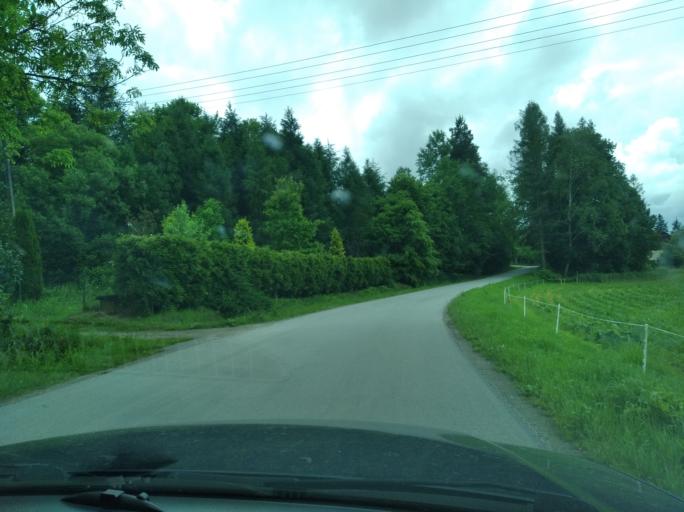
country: PL
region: Subcarpathian Voivodeship
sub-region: Powiat przemyski
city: Dubiecko
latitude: 49.8328
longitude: 22.3951
